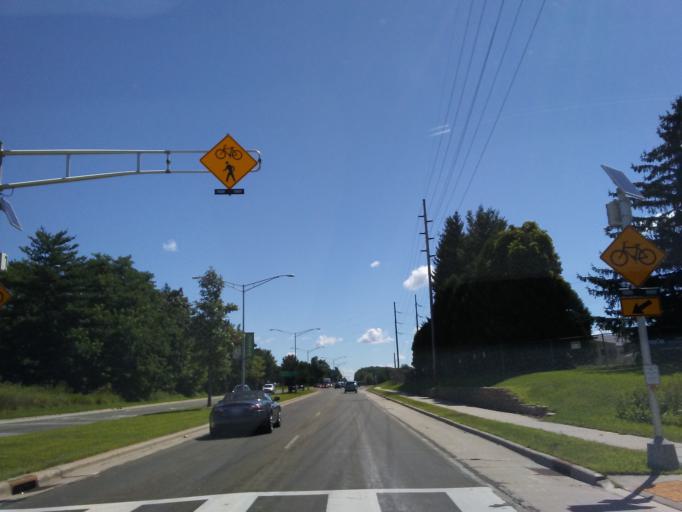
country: US
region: Wisconsin
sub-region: Dane County
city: Fitchburg
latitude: 43.0153
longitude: -89.4614
